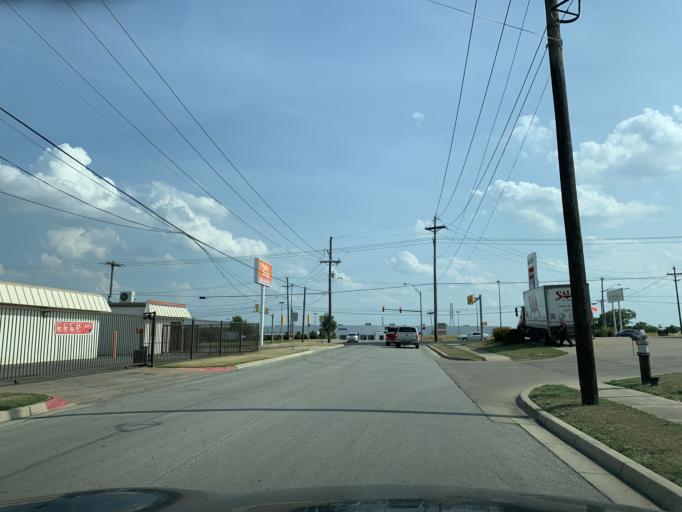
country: US
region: Texas
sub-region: Tarrant County
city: Richland Hills
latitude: 32.8098
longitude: -97.2161
